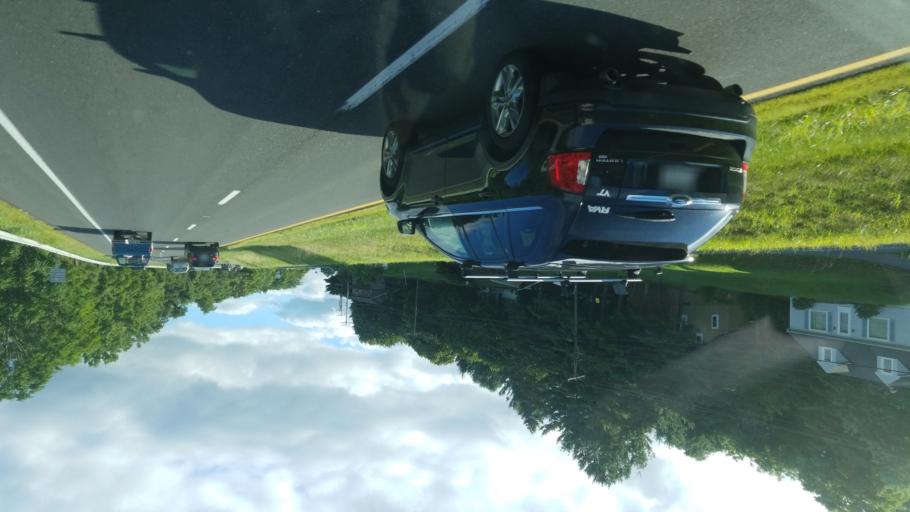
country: US
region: Virginia
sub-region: City of Winchester
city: Winchester
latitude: 39.2426
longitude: -78.2016
